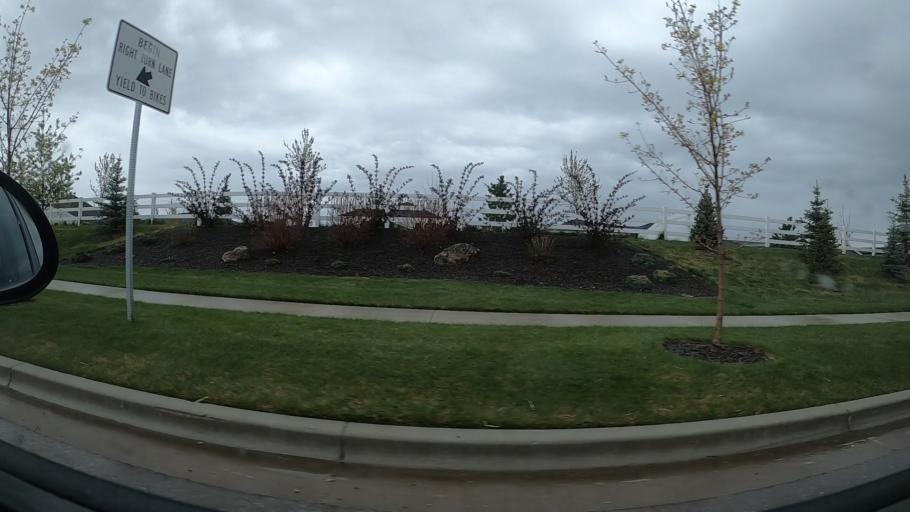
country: US
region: Idaho
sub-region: Ada County
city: Eagle
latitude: 43.7355
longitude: -116.2994
